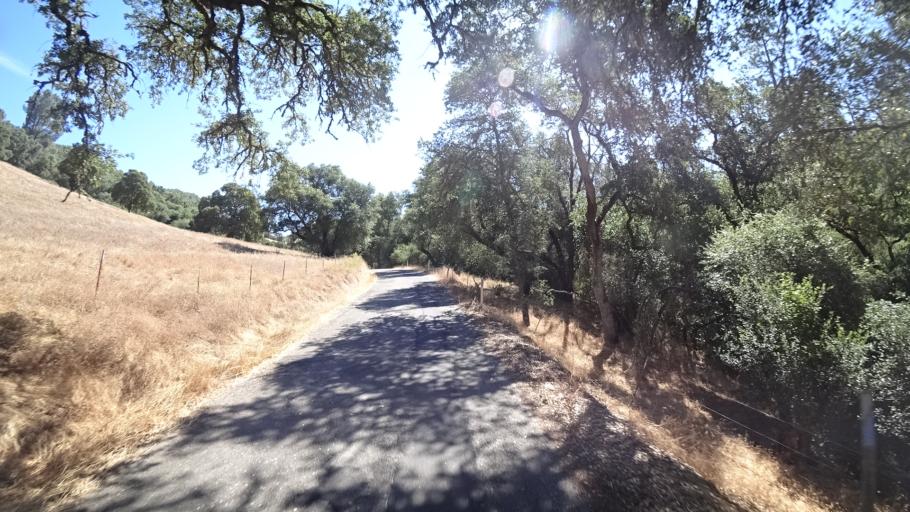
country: US
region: California
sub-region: Calaveras County
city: Angels Camp
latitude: 38.1462
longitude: -120.5661
